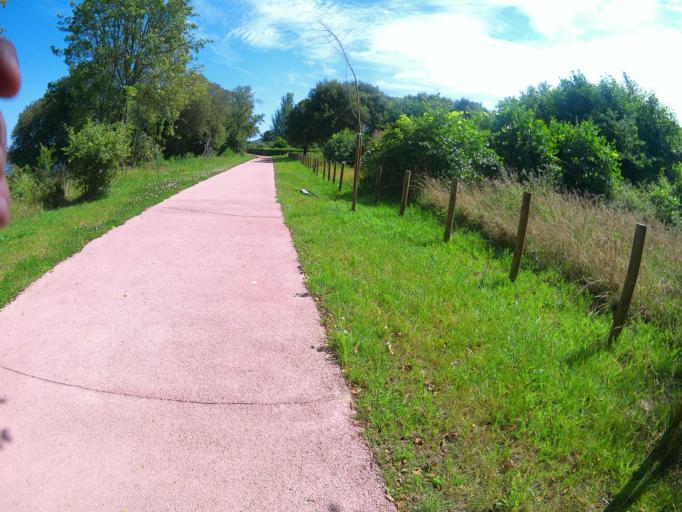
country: PT
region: Viana do Castelo
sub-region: Vila Nova de Cerveira
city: Vila Nova de Cerveira
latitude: 41.9188
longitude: -8.7773
